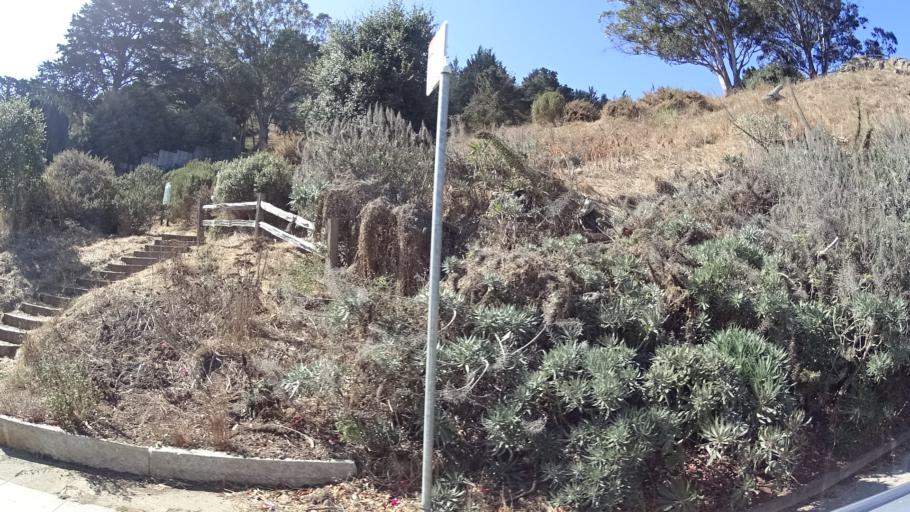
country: US
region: California
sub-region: San Francisco County
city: San Francisco
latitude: 37.7418
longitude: -122.4325
